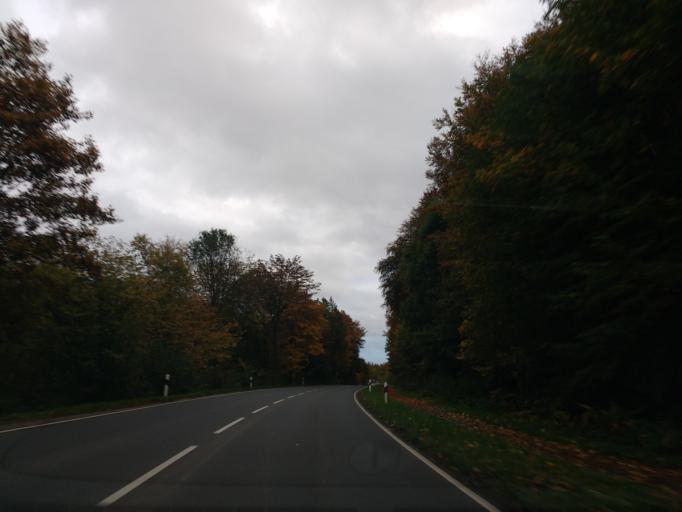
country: DE
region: Lower Saxony
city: Bad Lauterberg im Harz
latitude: 51.6055
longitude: 10.4492
